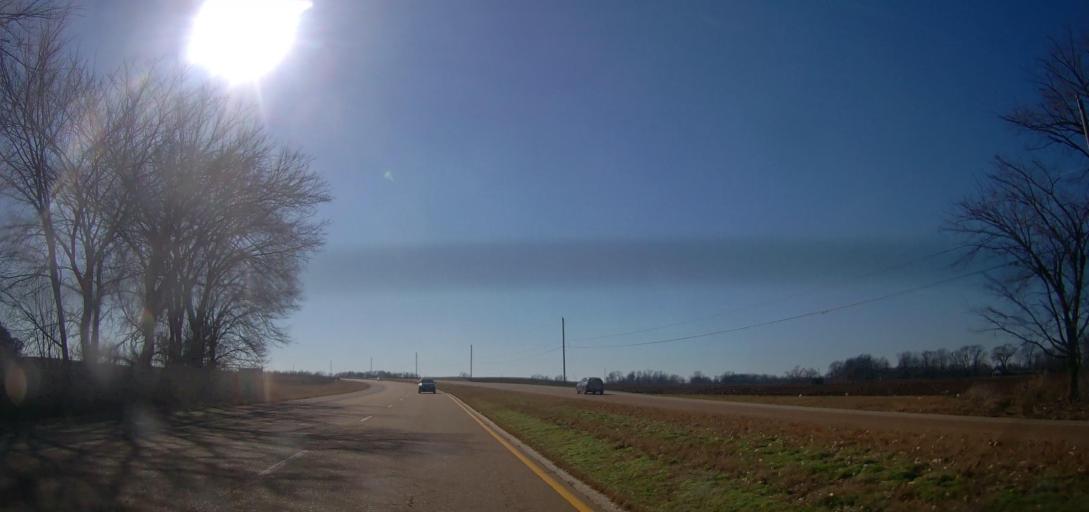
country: US
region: Tennessee
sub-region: Shelby County
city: Millington
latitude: 35.3120
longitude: -89.8797
